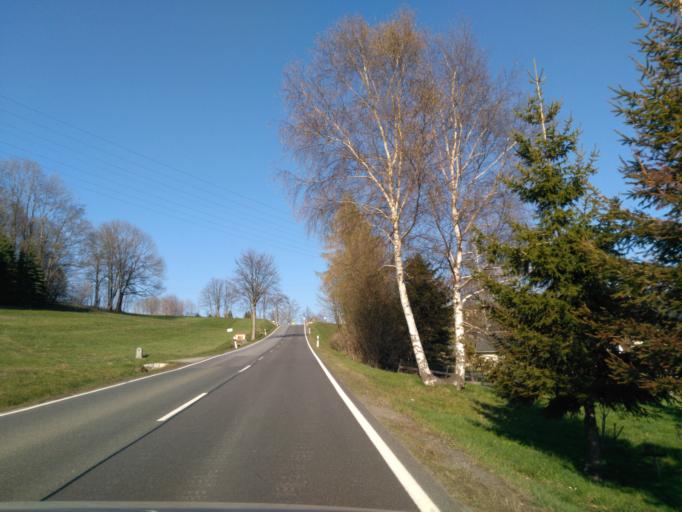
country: DE
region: Saxony
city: Scheibenberg
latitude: 50.5377
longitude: 12.9022
